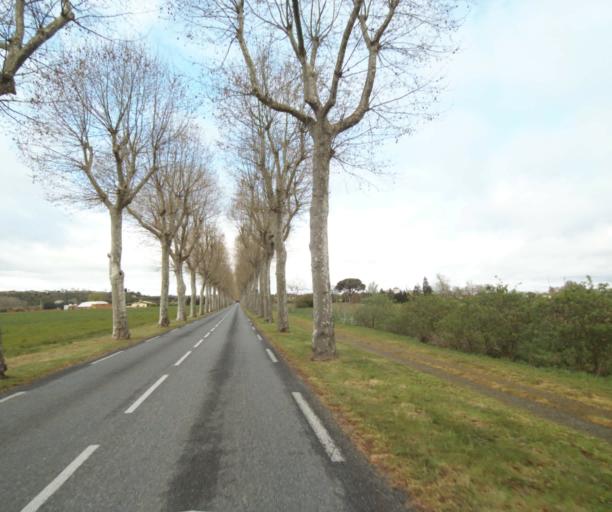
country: FR
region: Midi-Pyrenees
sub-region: Departement de l'Ariege
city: Saverdun
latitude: 43.2315
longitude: 1.5905
